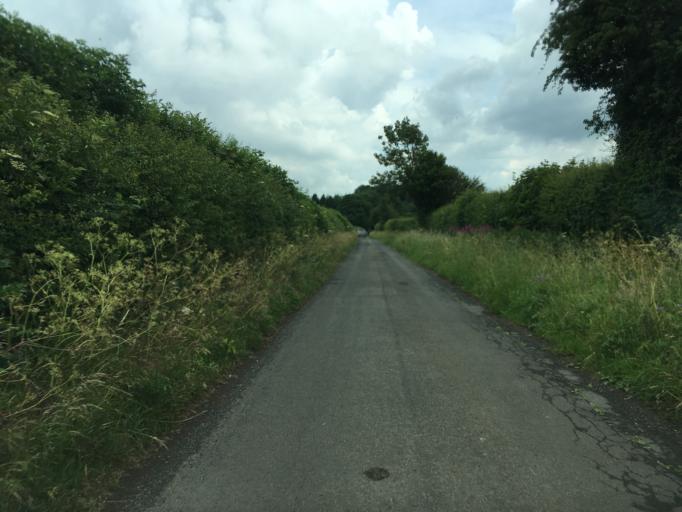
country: GB
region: England
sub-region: Gloucestershire
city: Shurdington
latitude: 51.8067
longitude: -2.0856
